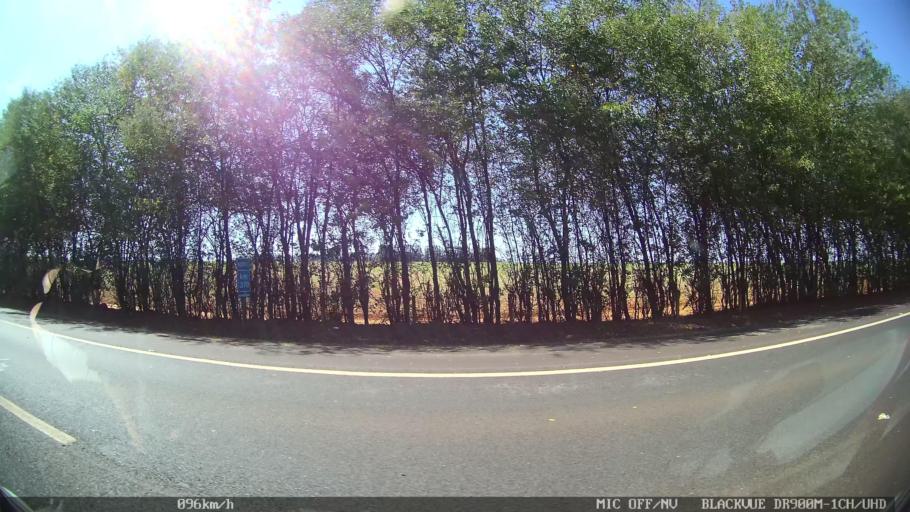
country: BR
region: Sao Paulo
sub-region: Batatais
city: Batatais
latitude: -20.7453
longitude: -47.5312
